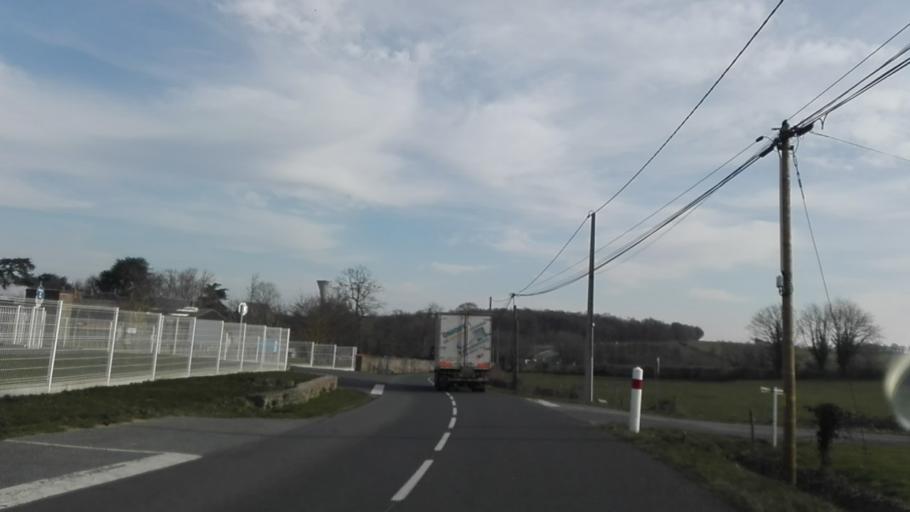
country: FR
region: Pays de la Loire
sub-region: Departement de la Vendee
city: Chavagnes-en-Paillers
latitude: 46.8989
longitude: -1.2338
